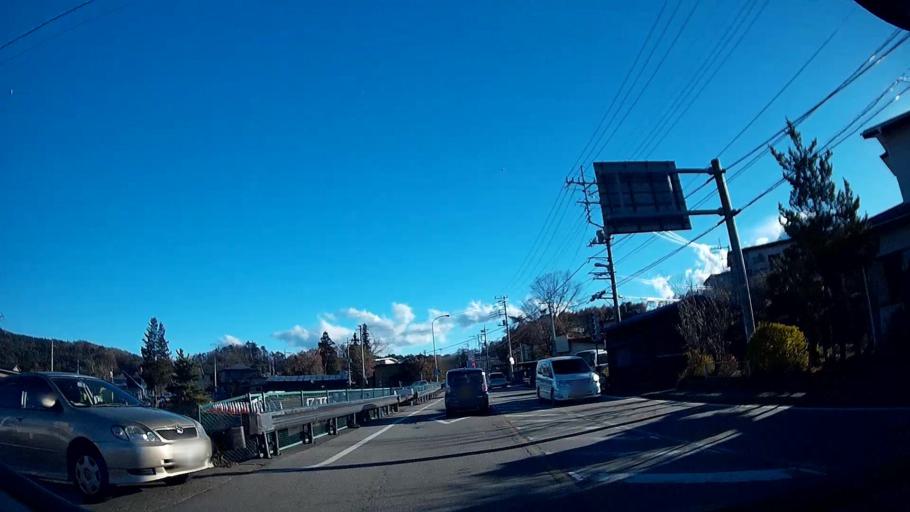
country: JP
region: Yamanashi
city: Fujikawaguchiko
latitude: 35.4627
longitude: 138.8038
